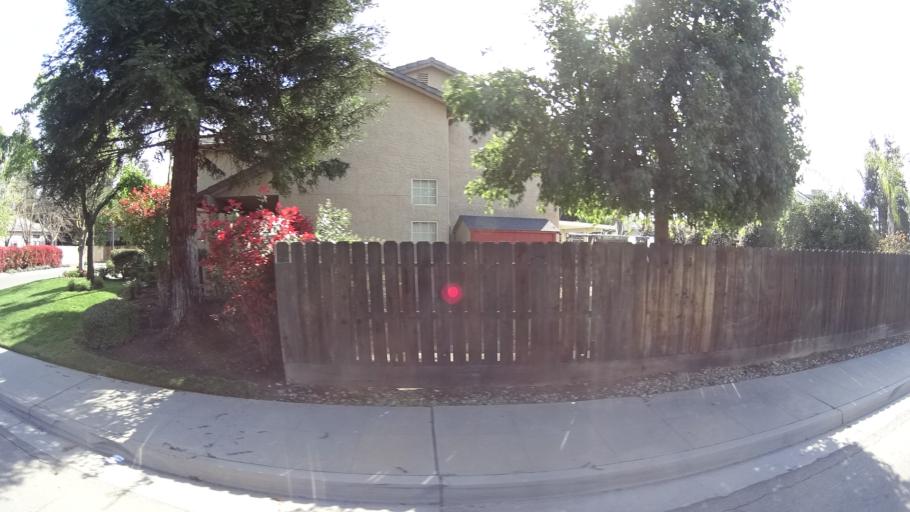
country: US
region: California
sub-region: Fresno County
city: West Park
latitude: 36.8408
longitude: -119.8776
